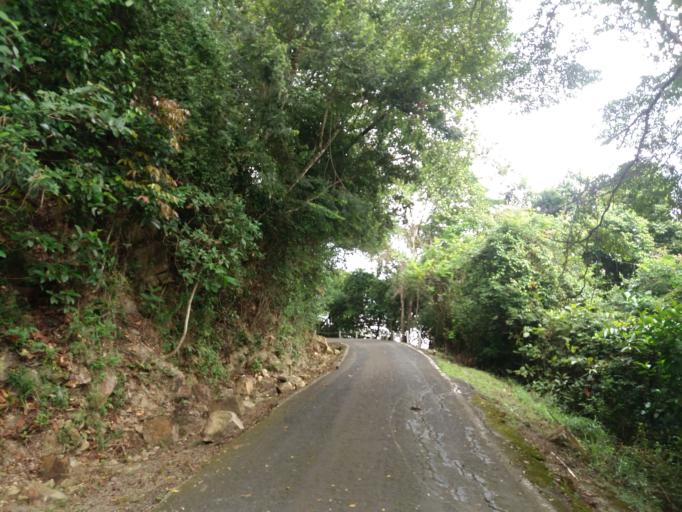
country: PA
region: Panama
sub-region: Distrito de Panama
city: Ancon
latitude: 8.9585
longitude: -79.5485
